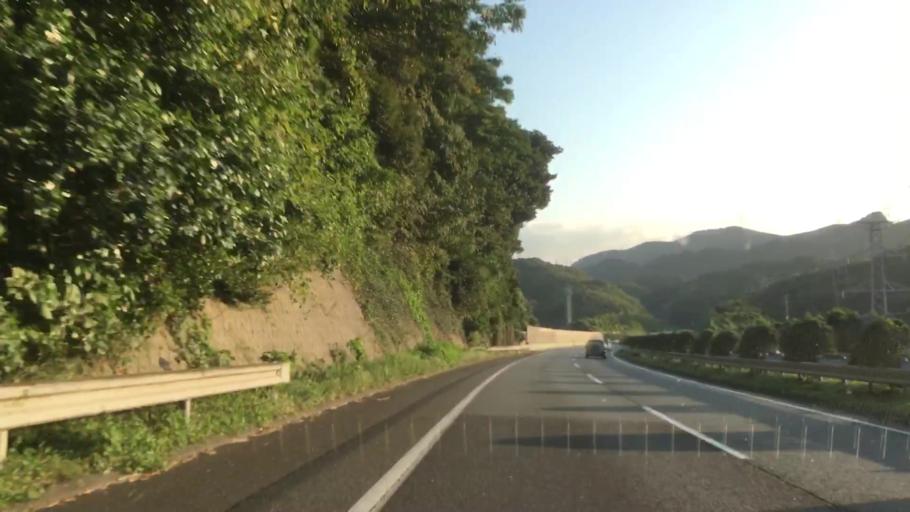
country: JP
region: Yamaguchi
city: Shimonoseki
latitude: 33.9106
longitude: 130.9753
